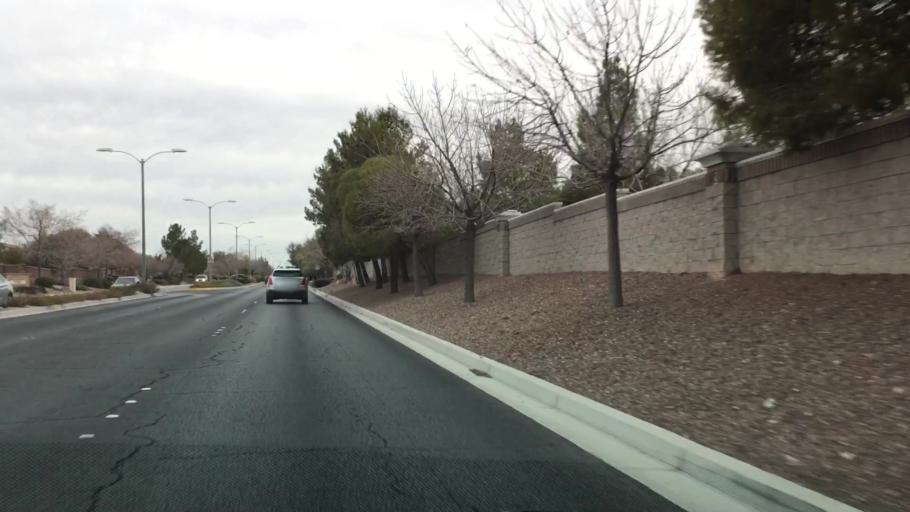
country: US
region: Nevada
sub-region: Clark County
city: Whitney
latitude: 35.9735
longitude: -115.1011
